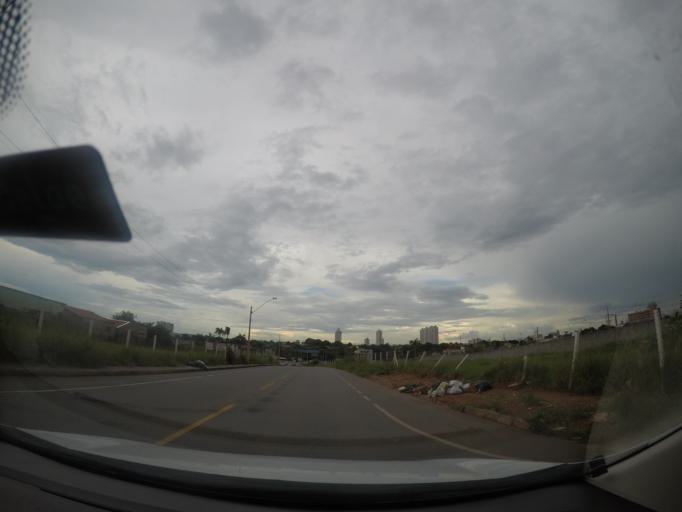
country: BR
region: Goias
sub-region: Goiania
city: Goiania
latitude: -16.6536
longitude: -49.2651
